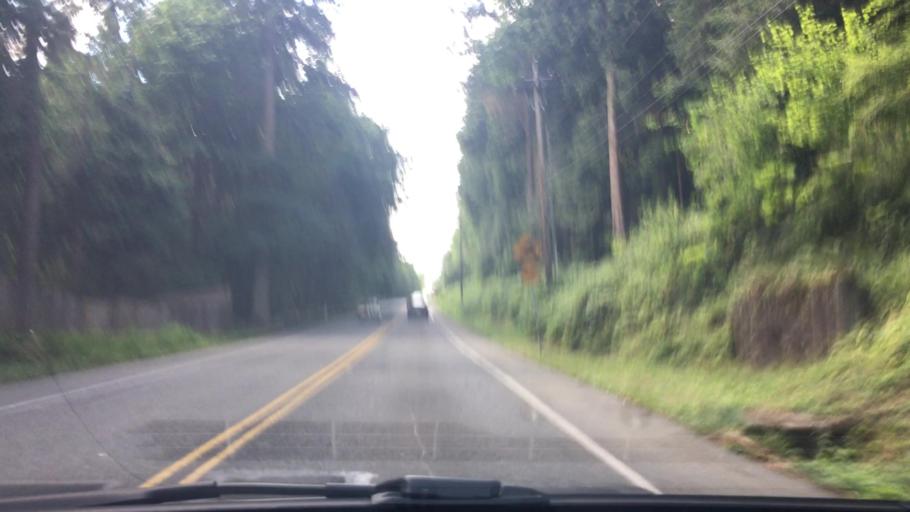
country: US
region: Washington
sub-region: King County
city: City of Sammamish
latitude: 47.5721
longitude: -122.0358
